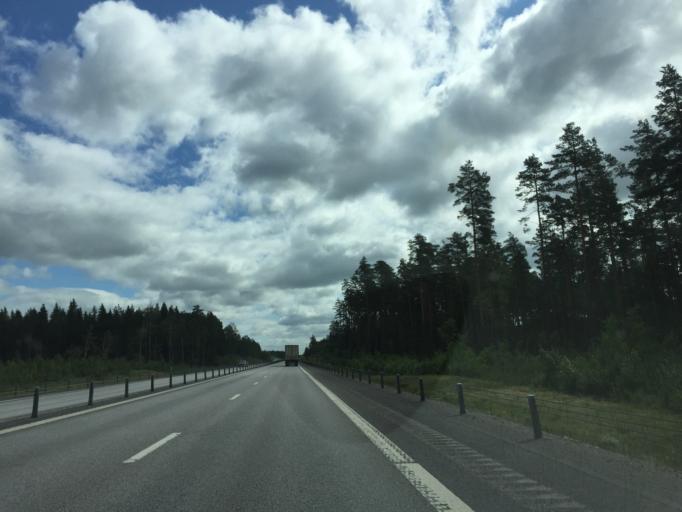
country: SE
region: OErebro
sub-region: Lekebergs Kommun
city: Fjugesta
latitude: 59.2522
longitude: 14.8534
